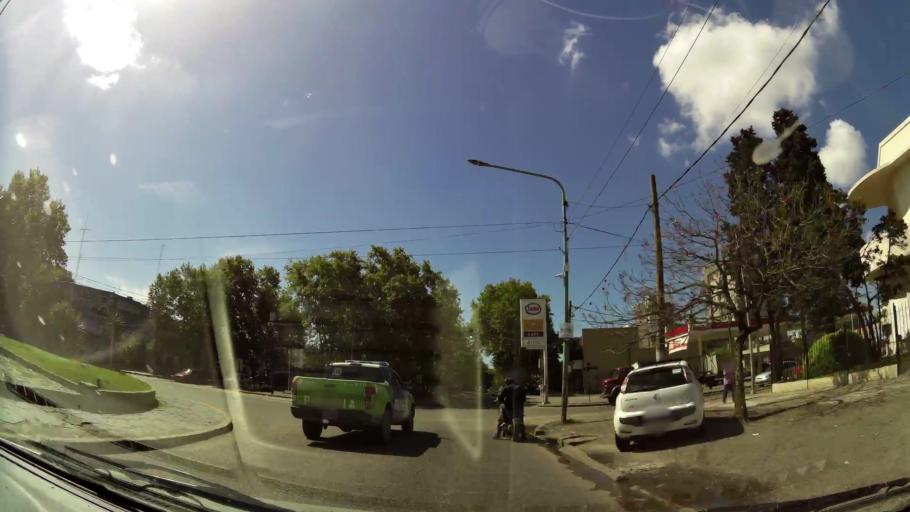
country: AR
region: Buenos Aires
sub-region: Partido de Quilmes
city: Quilmes
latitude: -34.8093
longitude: -58.2781
